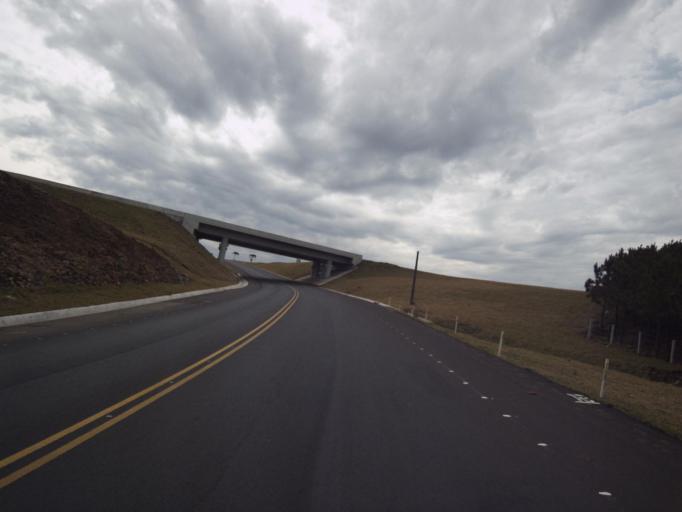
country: BR
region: Santa Catarina
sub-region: Cacador
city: Cacador
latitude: -26.6101
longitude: -51.4799
